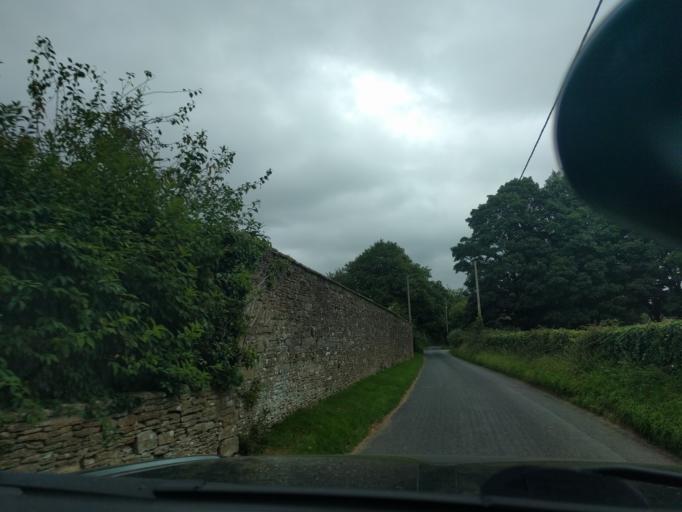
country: GB
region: England
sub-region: Wiltshire
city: Neston
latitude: 51.4121
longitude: -2.1876
